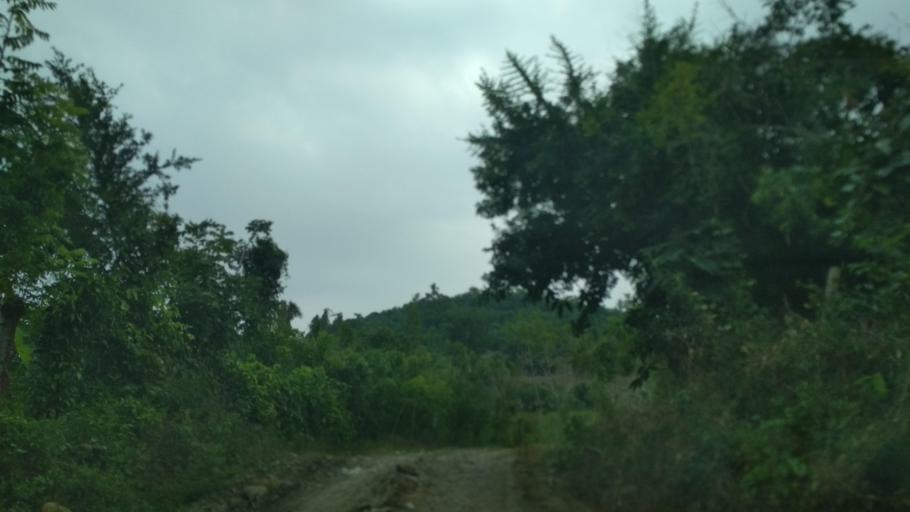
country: MM
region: Kayah
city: Loikaw
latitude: 20.2108
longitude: 97.3278
